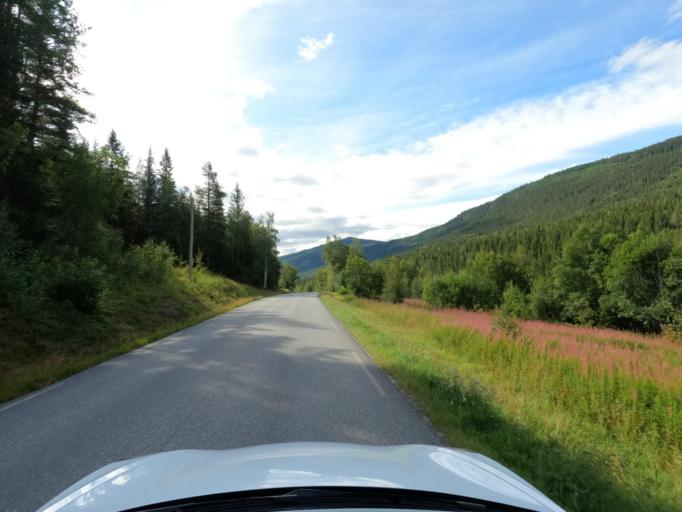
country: NO
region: Buskerud
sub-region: Nore og Uvdal
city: Rodberg
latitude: 60.0828
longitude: 8.7678
